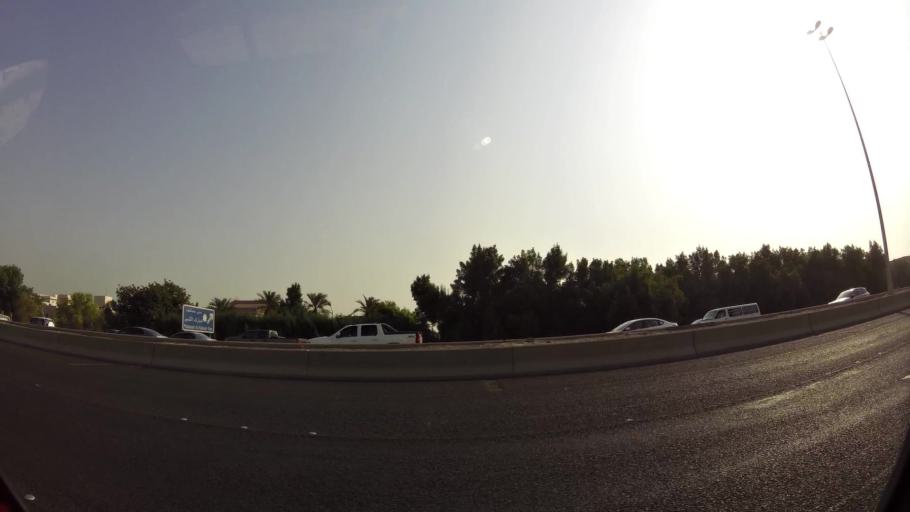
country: KW
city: Al Funaytis
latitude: 29.2041
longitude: 48.1057
